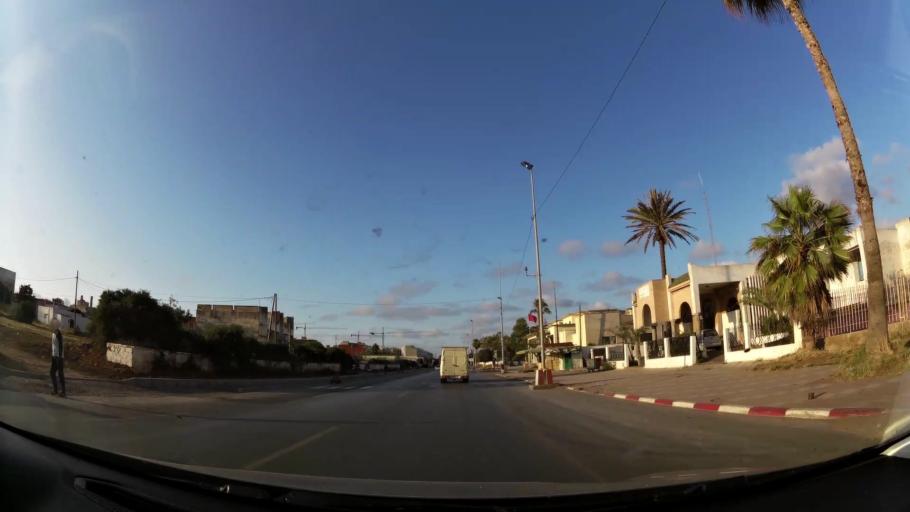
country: MA
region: Rabat-Sale-Zemmour-Zaer
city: Sale
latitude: 34.1215
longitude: -6.7404
